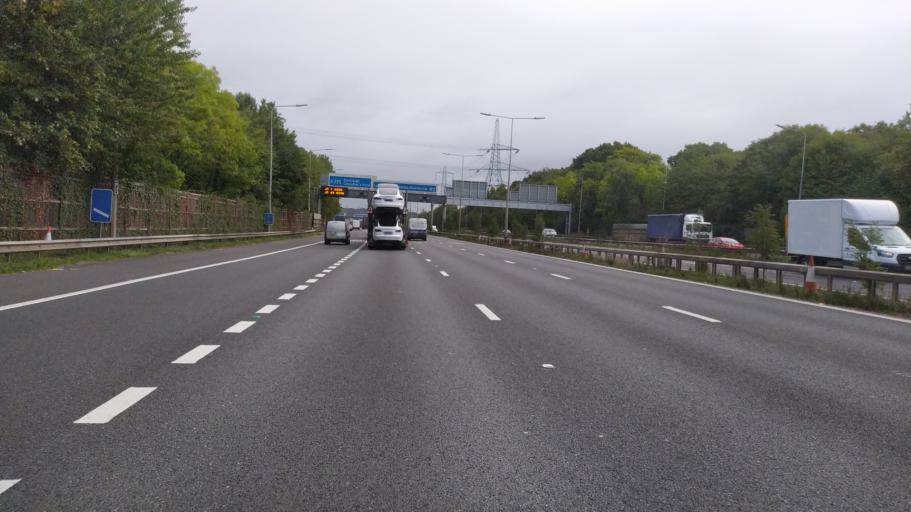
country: GB
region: England
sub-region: Hampshire
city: Eastleigh
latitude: 50.9670
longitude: -1.3816
